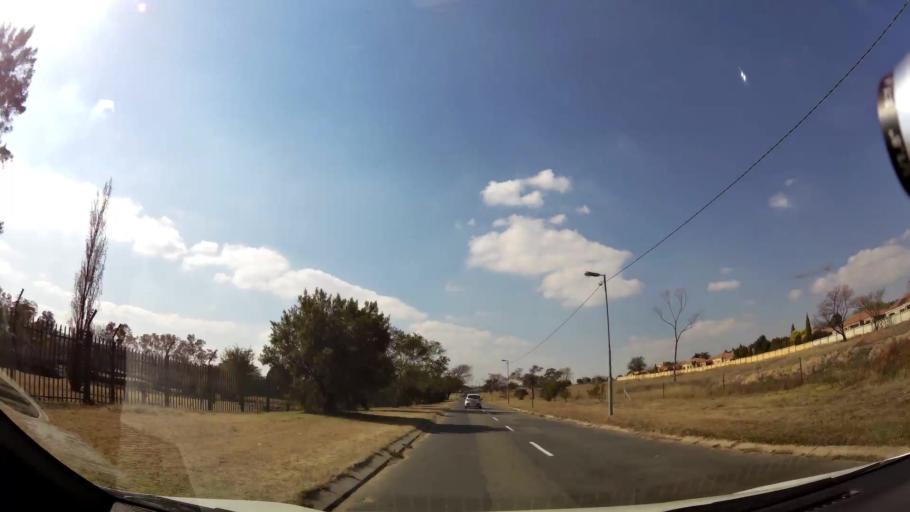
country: ZA
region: Gauteng
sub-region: City of Johannesburg Metropolitan Municipality
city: Midrand
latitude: -26.0085
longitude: 28.0712
